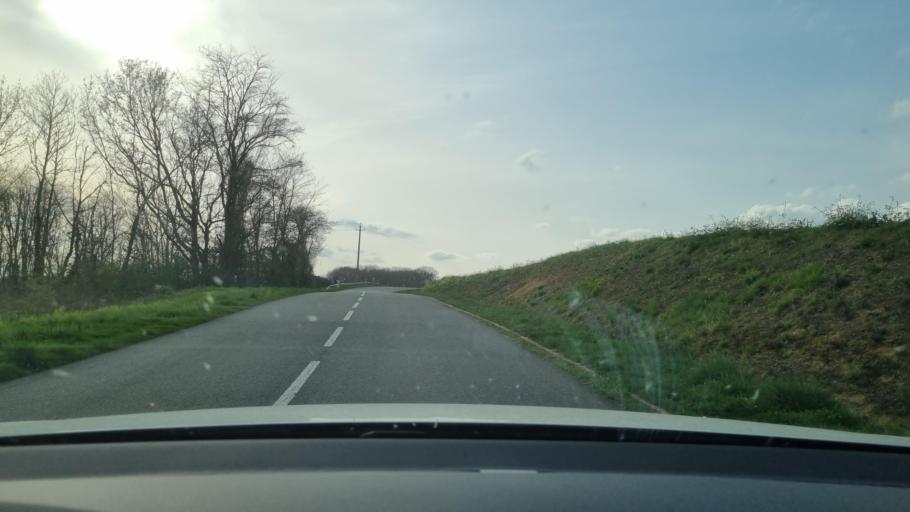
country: FR
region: Aquitaine
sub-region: Departement des Pyrenees-Atlantiques
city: Ger
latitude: 43.3737
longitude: -0.0831
